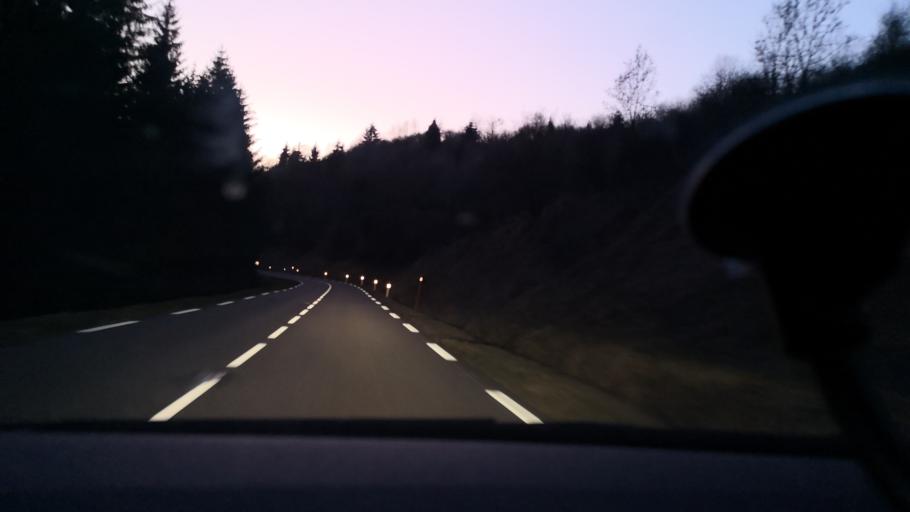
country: FR
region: Franche-Comte
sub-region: Departement du Jura
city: Champagnole
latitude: 46.7749
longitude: 5.9929
